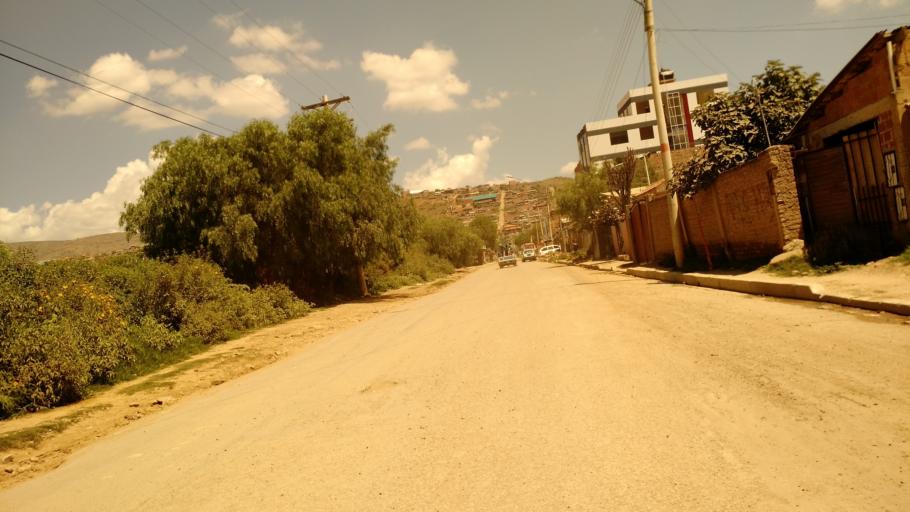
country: BO
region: Cochabamba
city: Cochabamba
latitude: -17.4559
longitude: -66.1567
